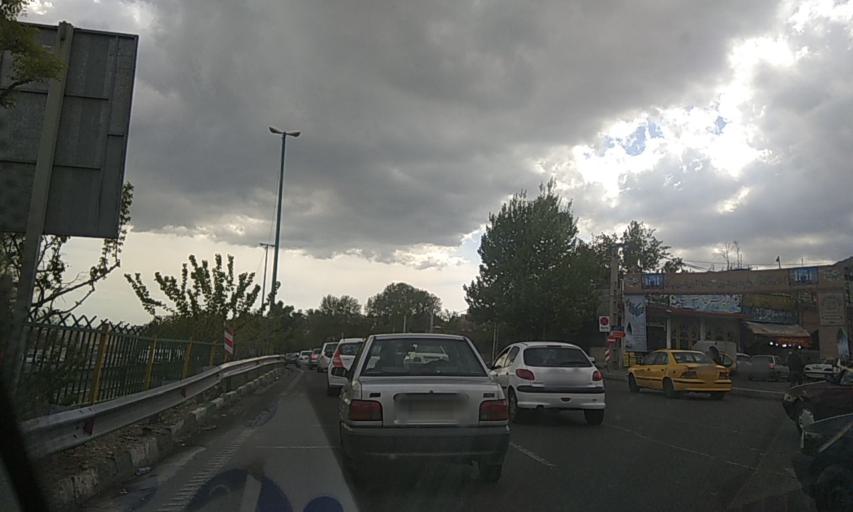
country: IR
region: Tehran
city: Tajrish
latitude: 35.7845
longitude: 51.3467
